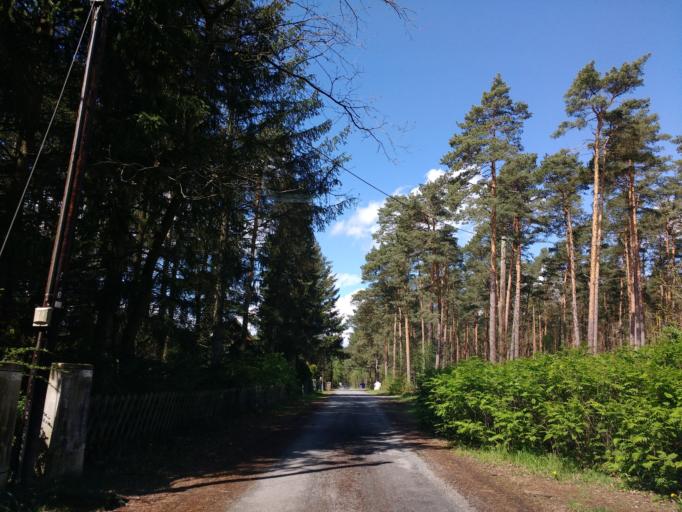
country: DE
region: Lower Saxony
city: Essel
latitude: 52.7075
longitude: 9.6747
